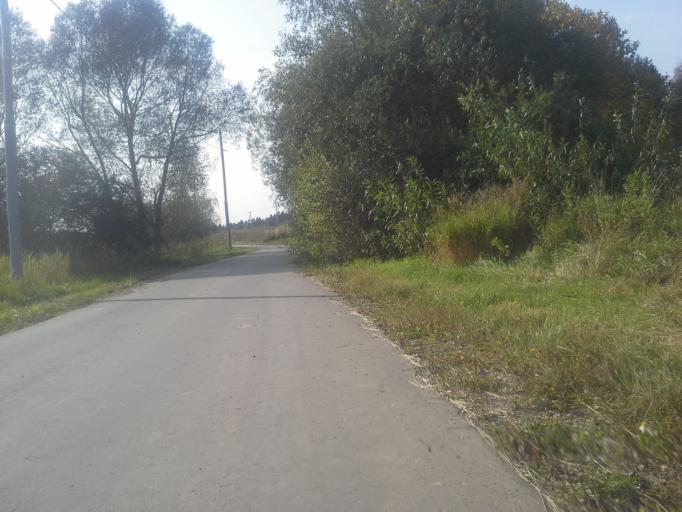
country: RU
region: Moskovskaya
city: Kievskij
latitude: 55.3972
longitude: 36.9720
